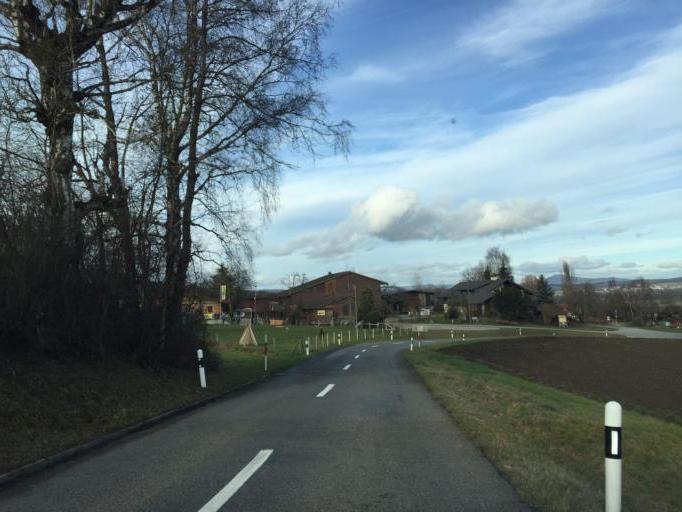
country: DE
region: Baden-Wuerttemberg
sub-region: Freiburg Region
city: Busingen
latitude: 47.6559
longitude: 8.6903
